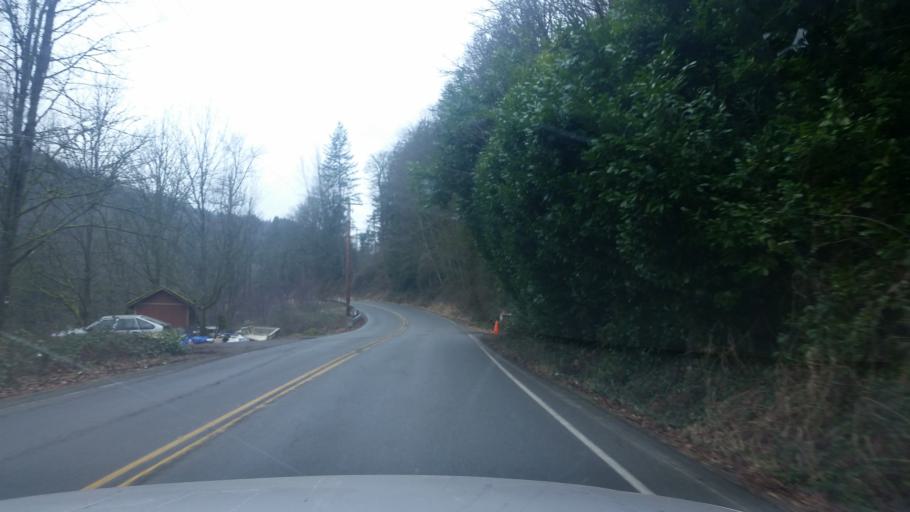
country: US
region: Washington
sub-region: King County
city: Issaquah
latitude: 47.5355
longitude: -121.9752
